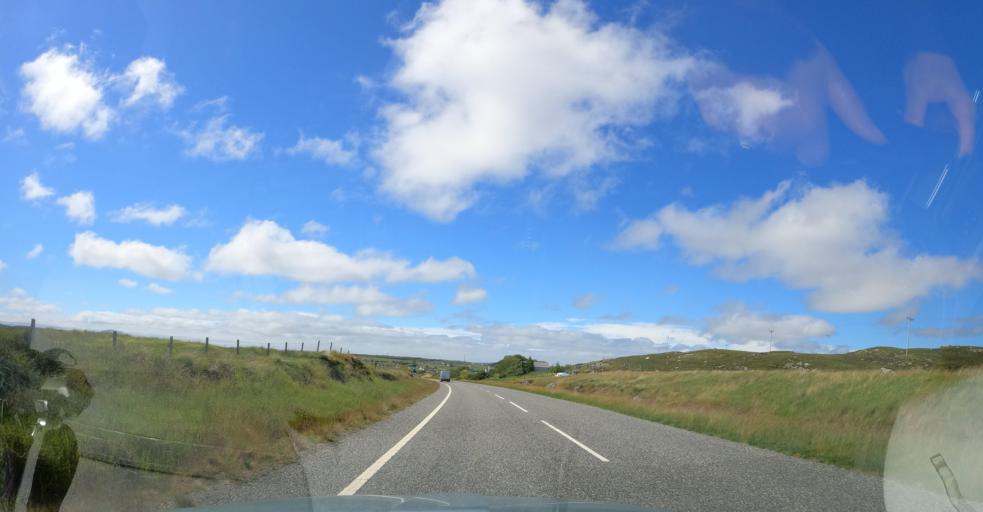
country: GB
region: Scotland
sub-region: Eilean Siar
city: Harris
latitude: 58.1963
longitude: -6.7196
